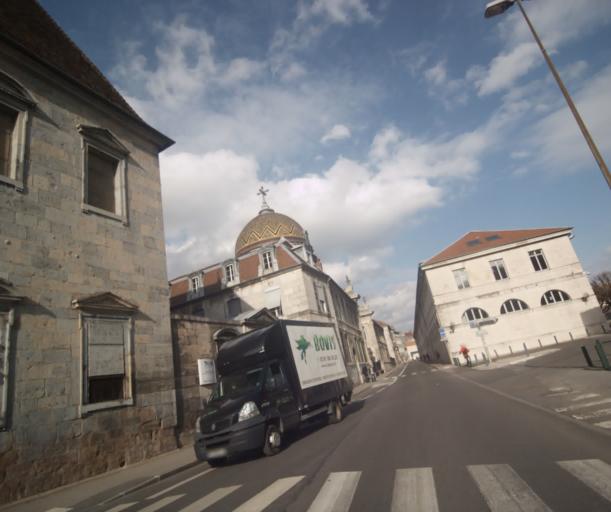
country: FR
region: Franche-Comte
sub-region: Departement du Doubs
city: Besancon
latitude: 47.2351
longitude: 6.0211
